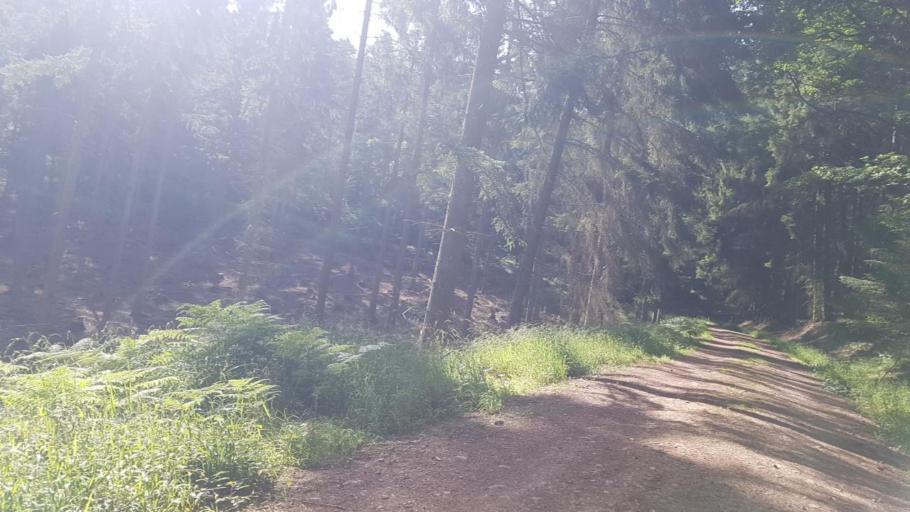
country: DE
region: North Rhine-Westphalia
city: Heimbach
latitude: 50.6189
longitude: 6.5062
